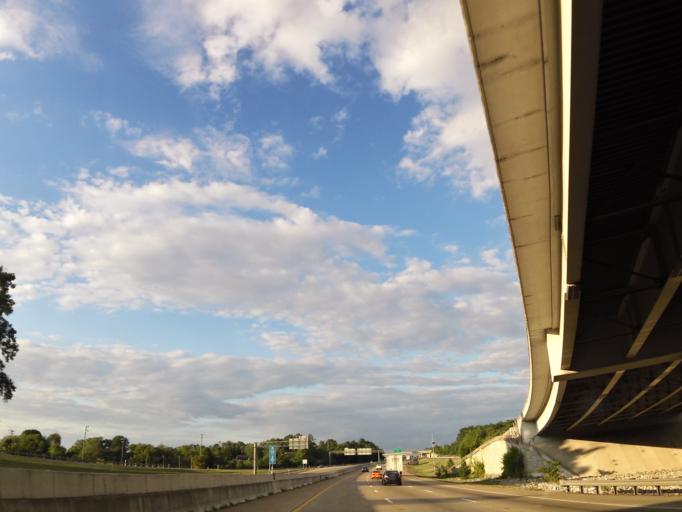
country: US
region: Tennessee
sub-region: Hamilton County
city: East Brainerd
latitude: 35.0279
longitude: -85.1723
